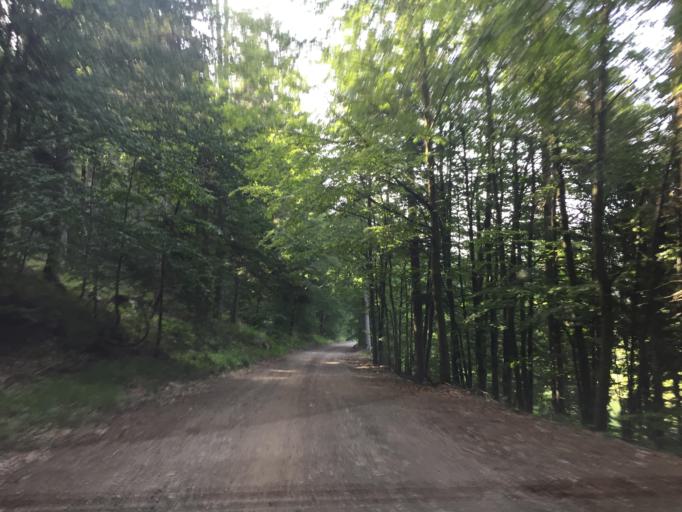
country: HR
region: Primorsko-Goranska
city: Klana
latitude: 45.4920
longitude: 14.4566
